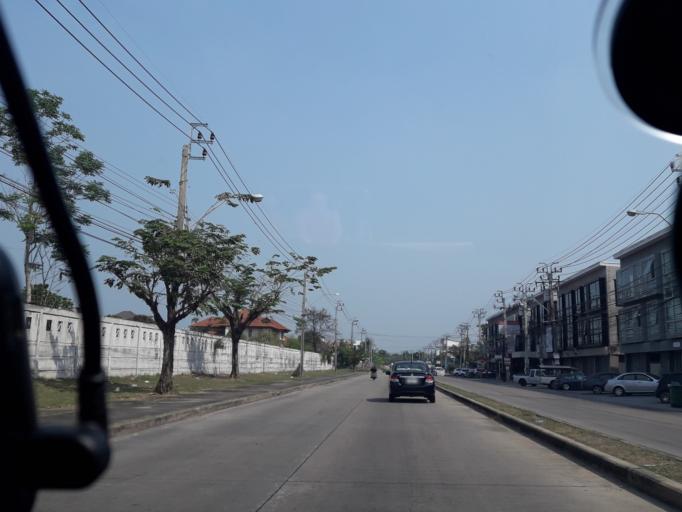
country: TH
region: Bangkok
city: Khan Na Yao
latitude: 13.8528
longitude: 100.7030
